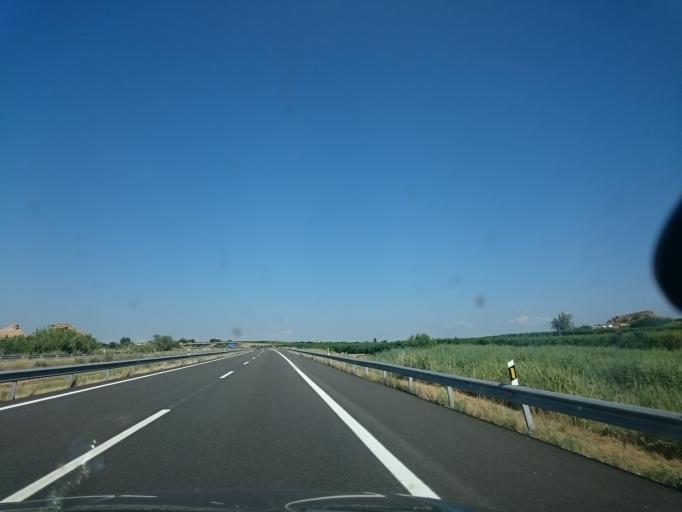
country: ES
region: Aragon
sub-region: Provincia de Huesca
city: Fraga
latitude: 41.4930
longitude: 0.3684
